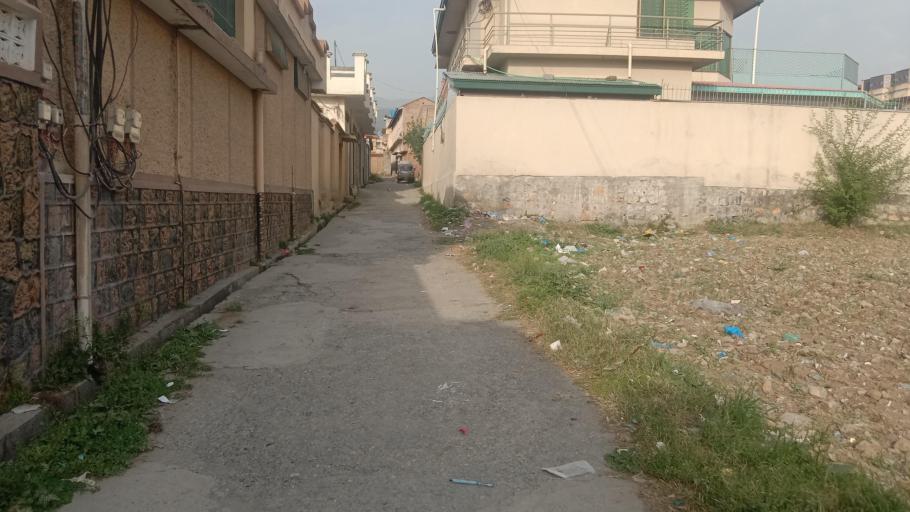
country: PK
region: Khyber Pakhtunkhwa
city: Abbottabad
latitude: 34.1631
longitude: 73.2622
